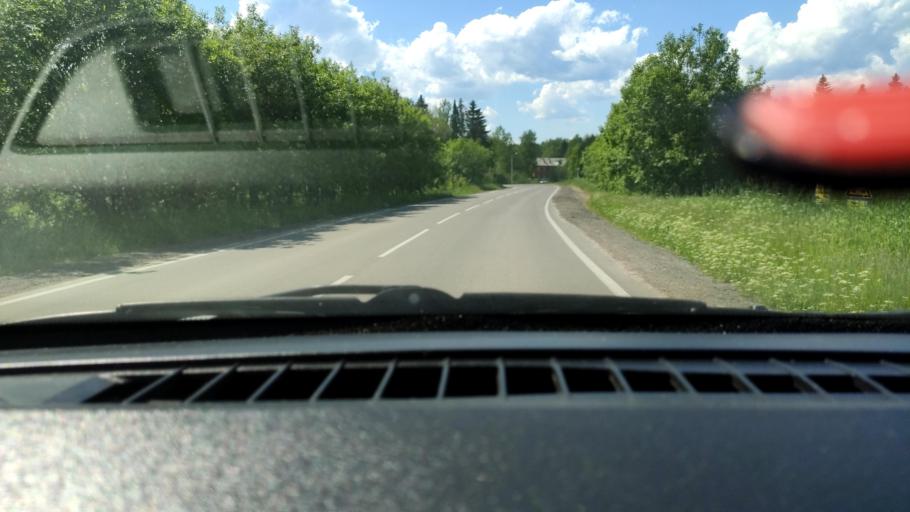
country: RU
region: Perm
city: Sylva
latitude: 58.0140
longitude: 56.7555
